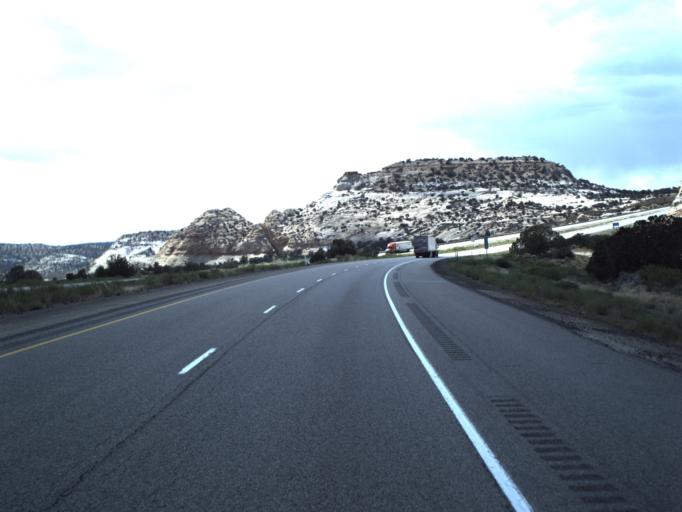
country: US
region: Utah
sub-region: Emery County
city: Ferron
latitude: 38.8476
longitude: -110.8895
